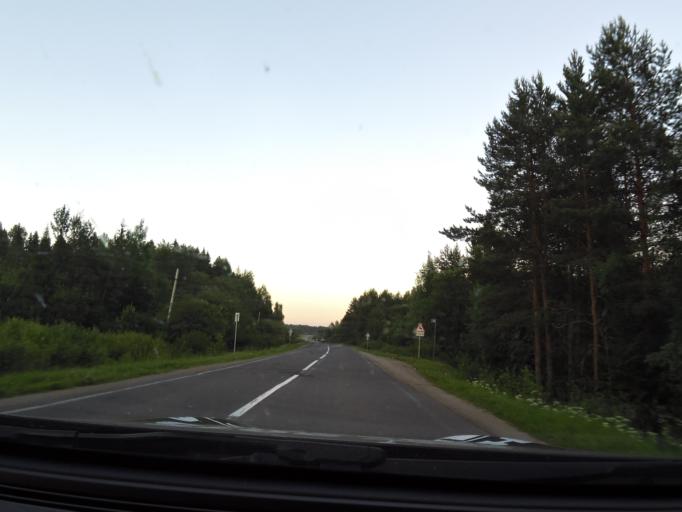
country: RU
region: Jaroslavl
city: Lyubim
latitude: 58.3337
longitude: 40.8936
